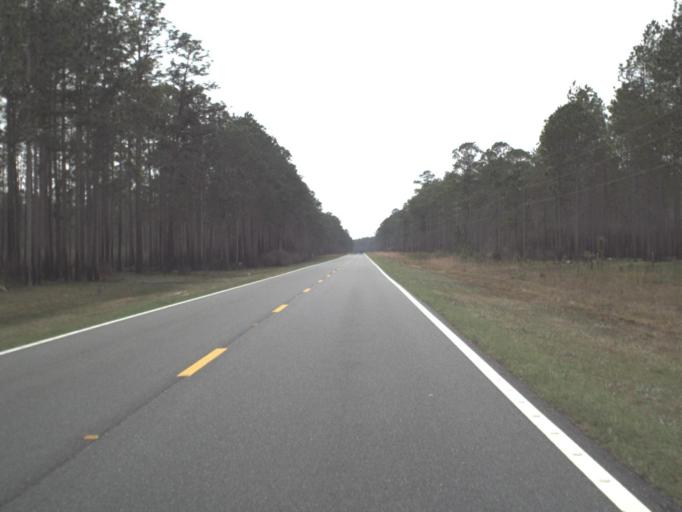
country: US
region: Florida
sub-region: Liberty County
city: Bristol
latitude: 30.1949
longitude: -84.9206
